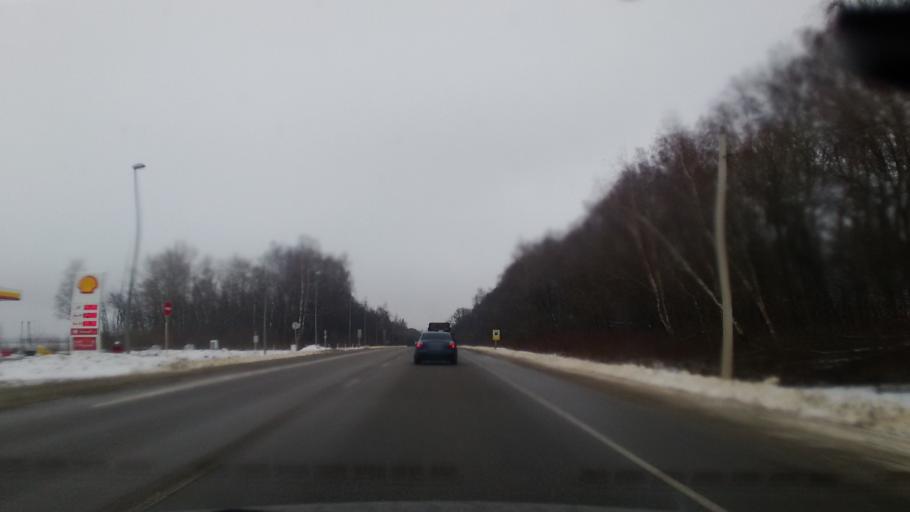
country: RU
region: Tula
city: Kireyevsk
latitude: 54.0201
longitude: 37.9126
